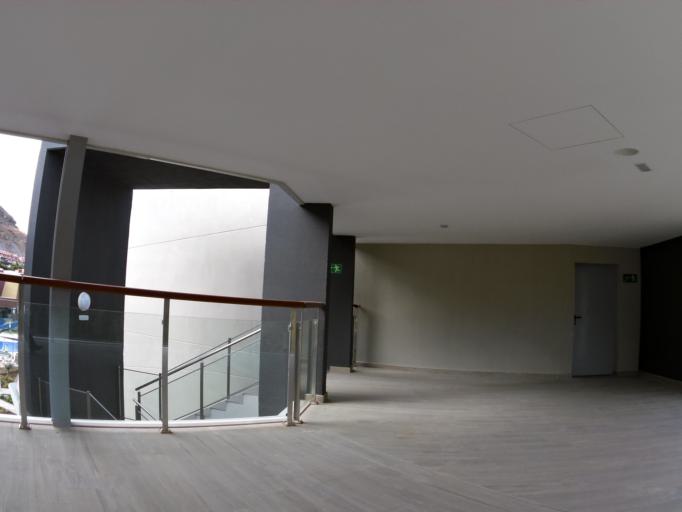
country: ES
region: Canary Islands
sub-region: Provincia de Las Palmas
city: Puerto Rico
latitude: 27.8274
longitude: -15.7574
